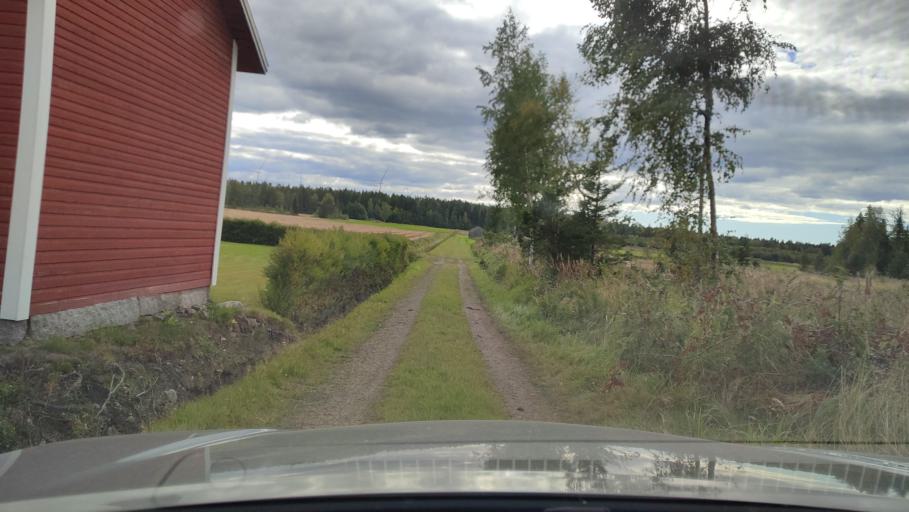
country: FI
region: Southern Ostrobothnia
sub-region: Suupohja
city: Karijoki
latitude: 62.2132
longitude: 21.5675
